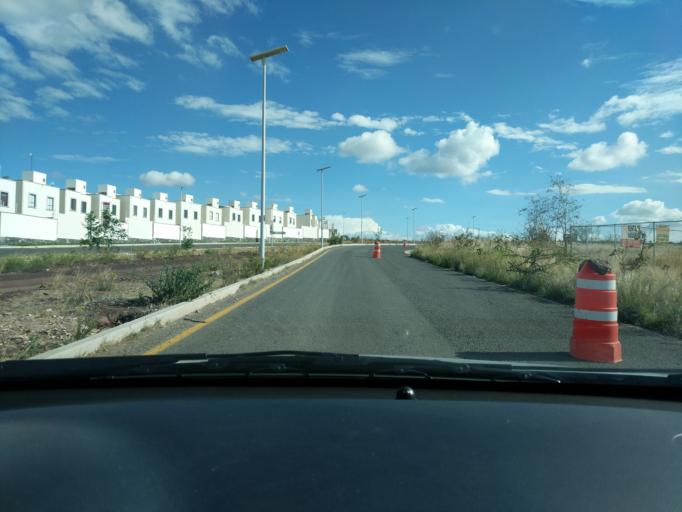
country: MX
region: Queretaro
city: La Canada
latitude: 20.5981
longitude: -100.2936
